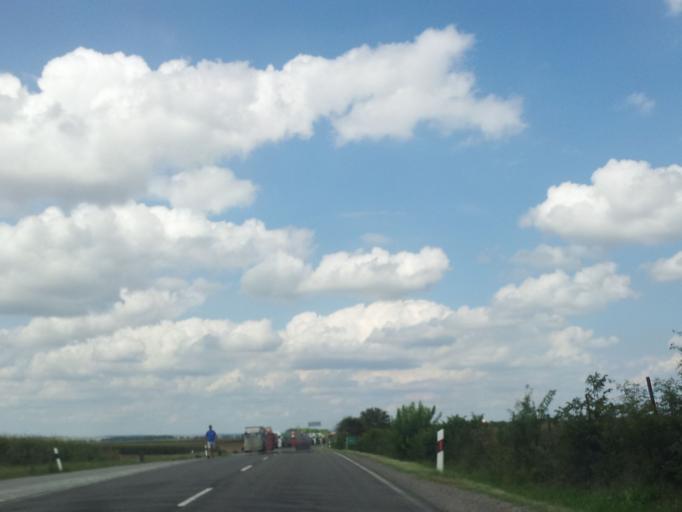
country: HU
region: Baranya
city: Mohacs
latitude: 45.9077
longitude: 18.6596
